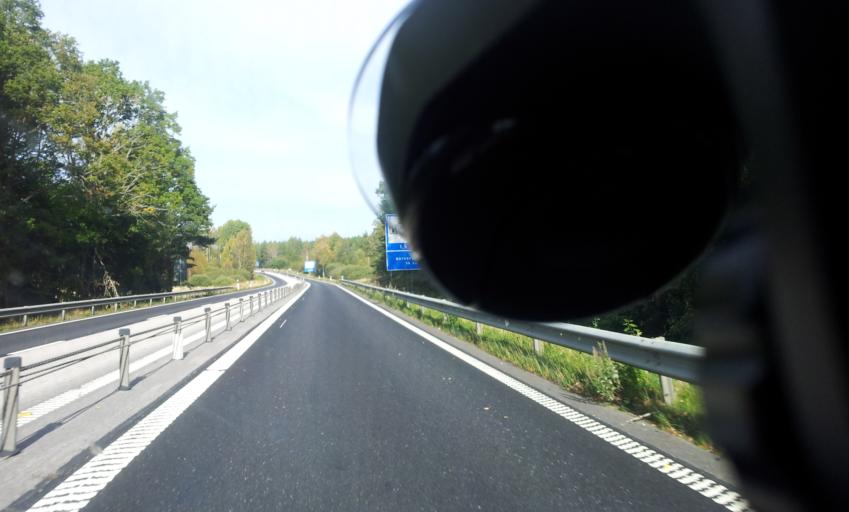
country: SE
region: Kalmar
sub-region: Oskarshamns Kommun
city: Oskarshamn
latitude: 57.3554
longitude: 16.4932
